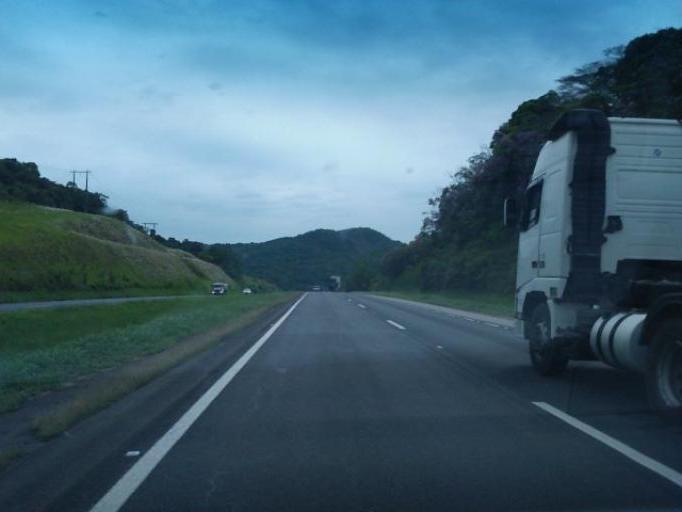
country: BR
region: Sao Paulo
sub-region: Juquia
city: Juquia
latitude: -24.3527
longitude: -47.6581
